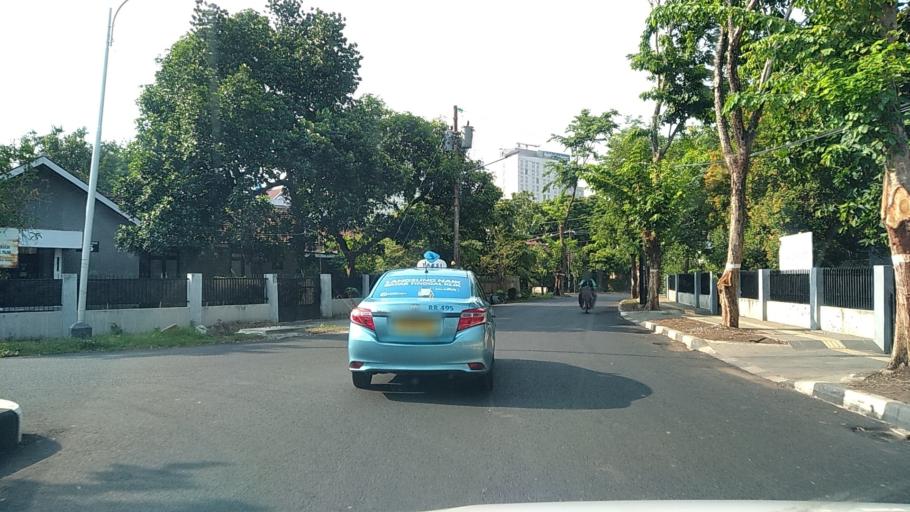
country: ID
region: Central Java
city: Semarang
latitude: -6.9944
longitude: 110.4261
